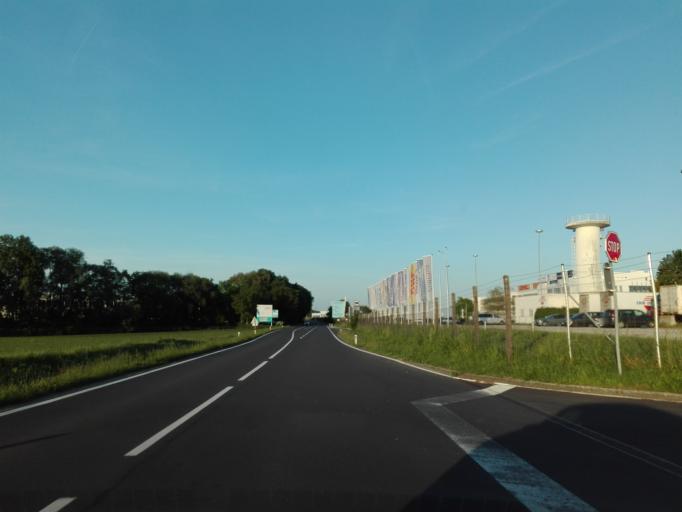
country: AT
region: Upper Austria
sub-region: Politischer Bezirk Linz-Land
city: Horsching
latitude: 48.2398
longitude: 14.1797
